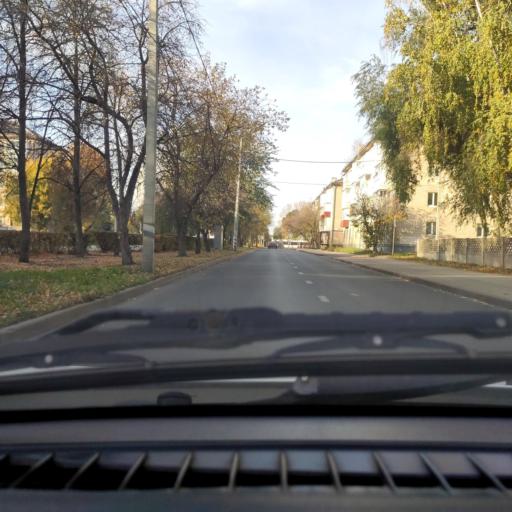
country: RU
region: Samara
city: Tol'yatti
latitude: 53.5061
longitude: 49.4128
